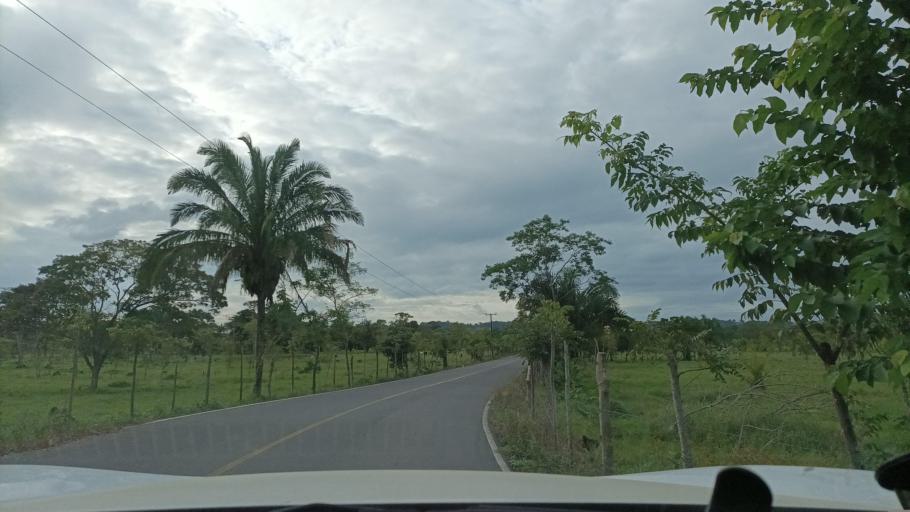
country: MX
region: Veracruz
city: Hidalgotitlan
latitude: 17.7382
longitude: -94.4879
